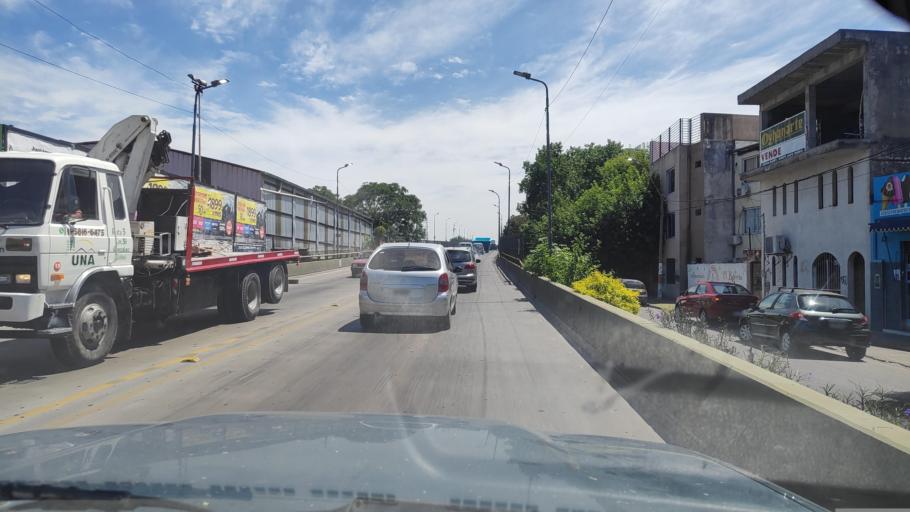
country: AR
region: Buenos Aires
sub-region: Partido de Moron
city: Moron
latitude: -34.6514
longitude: -58.6294
